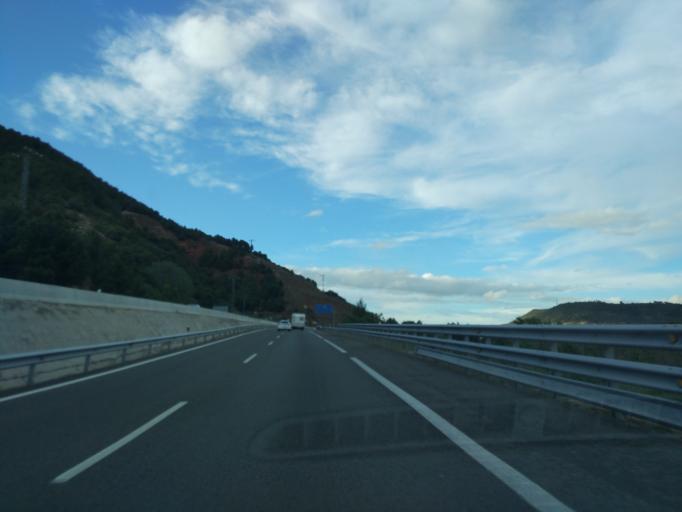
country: ES
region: Castille-La Mancha
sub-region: Provincia de Guadalajara
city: Tortola de Henares
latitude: 40.6796
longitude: -3.0961
